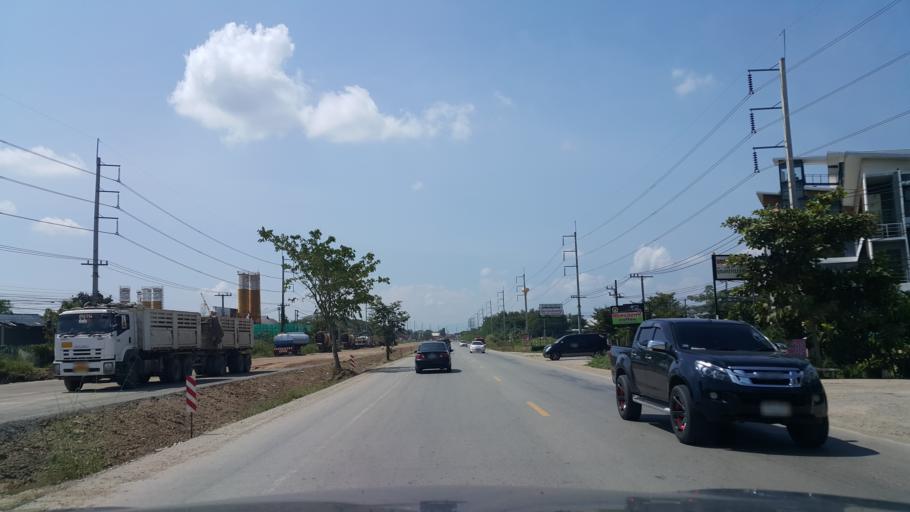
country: TH
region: Chiang Mai
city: Saraphi
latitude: 18.7245
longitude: 99.0127
